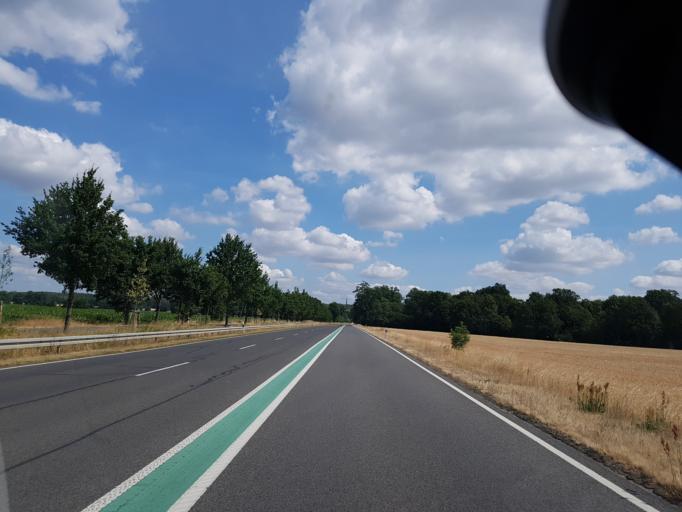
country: DE
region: Brandenburg
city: Drebkau
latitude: 51.6850
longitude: 14.2605
